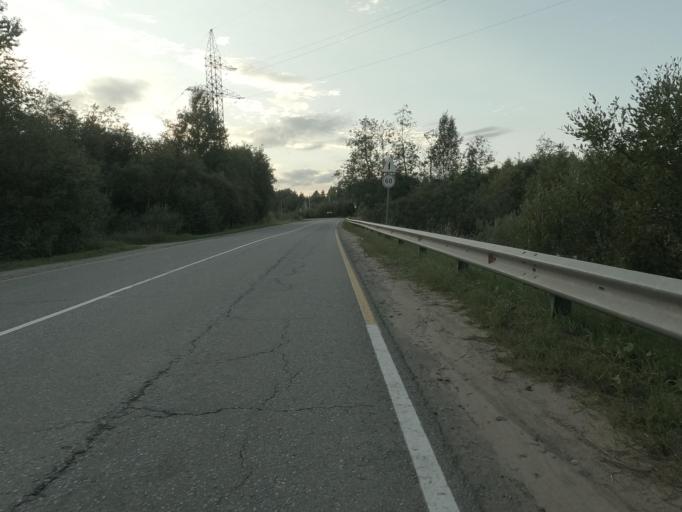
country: RU
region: Leningrad
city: Mga
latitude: 59.7589
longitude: 31.0177
